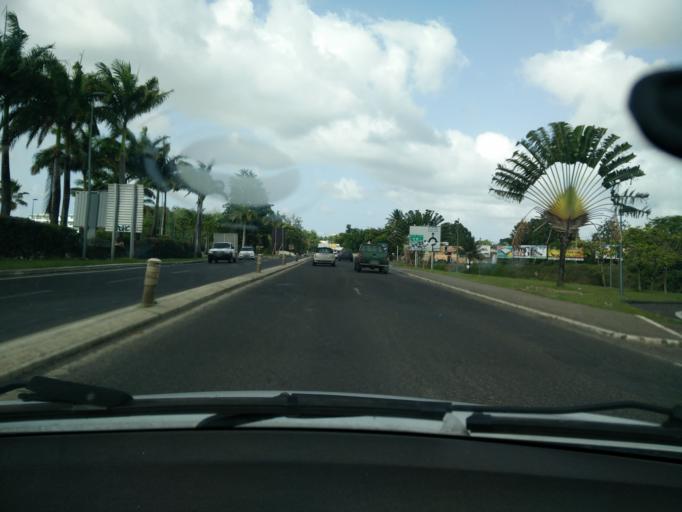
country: GP
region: Guadeloupe
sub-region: Guadeloupe
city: Les Abymes
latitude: 16.2641
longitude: -61.5123
